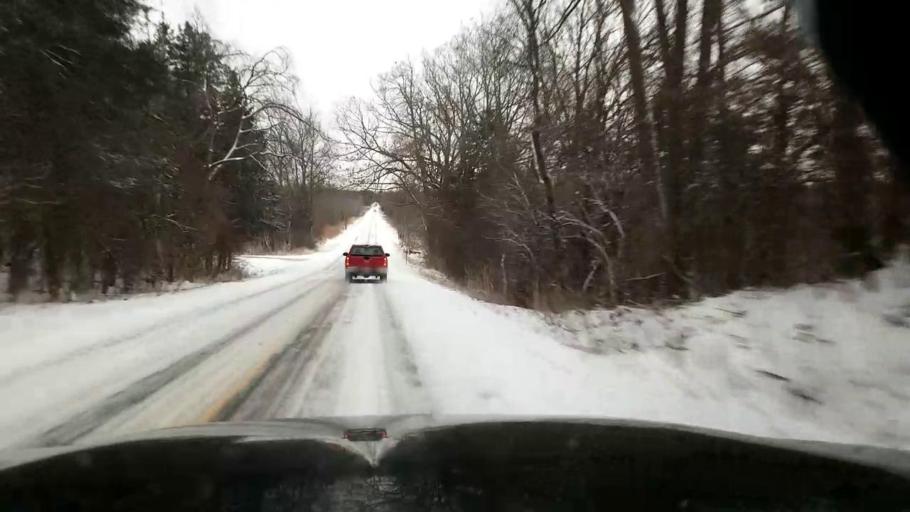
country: US
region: Michigan
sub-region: Jackson County
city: Spring Arbor
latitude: 42.1315
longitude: -84.4985
